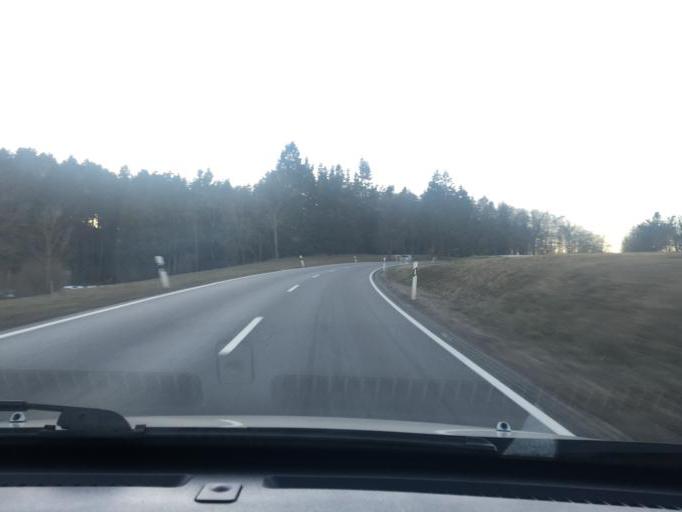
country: DE
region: Baden-Wuerttemberg
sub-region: Tuebingen Region
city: Rot an der Rot
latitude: 48.0522
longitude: 10.0411
